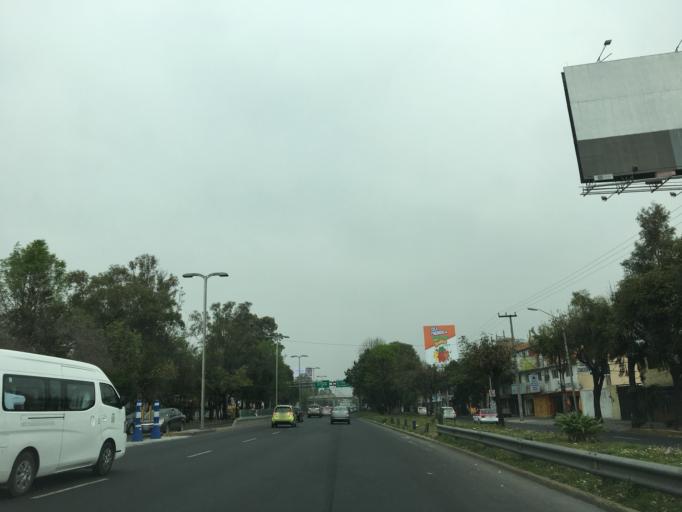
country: MX
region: Mexico City
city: Tlalpan
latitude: 19.2941
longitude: -99.1468
